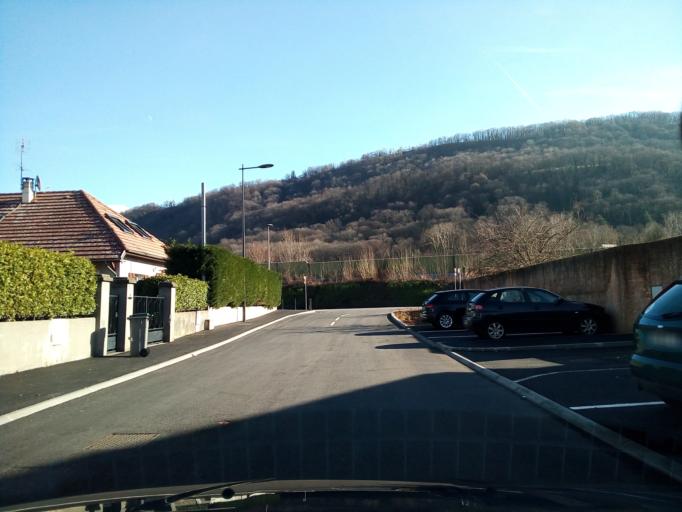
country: FR
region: Rhone-Alpes
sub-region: Departement de l'Isere
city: Saint-Martin-d'Heres
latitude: 45.1777
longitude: 5.7708
